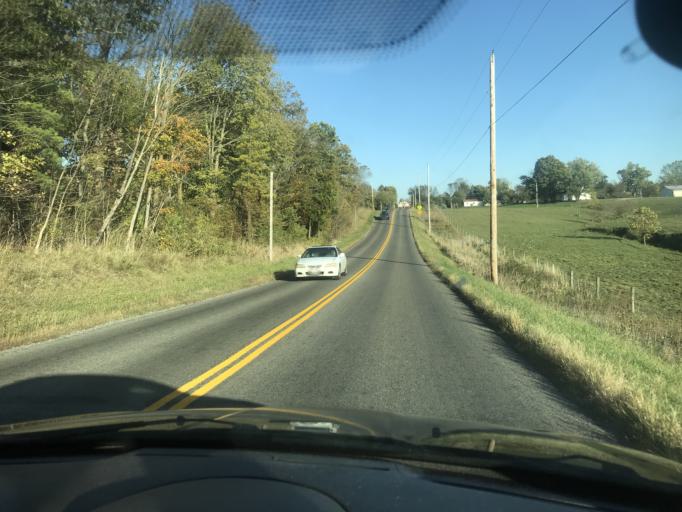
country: US
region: Ohio
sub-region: Logan County
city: Bellefontaine
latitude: 40.3326
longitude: -83.7709
